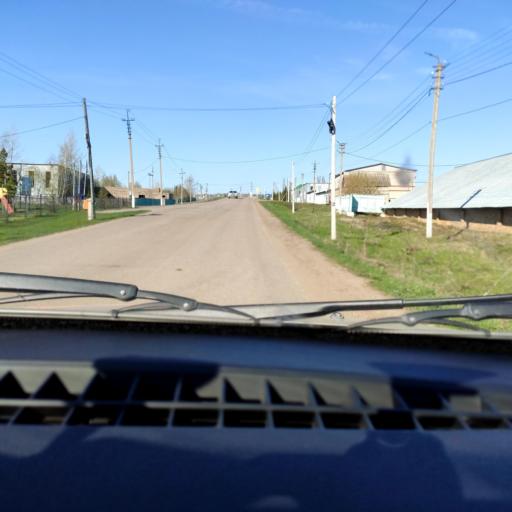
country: RU
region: Bashkortostan
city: Kabakovo
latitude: 54.5962
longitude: 56.1802
